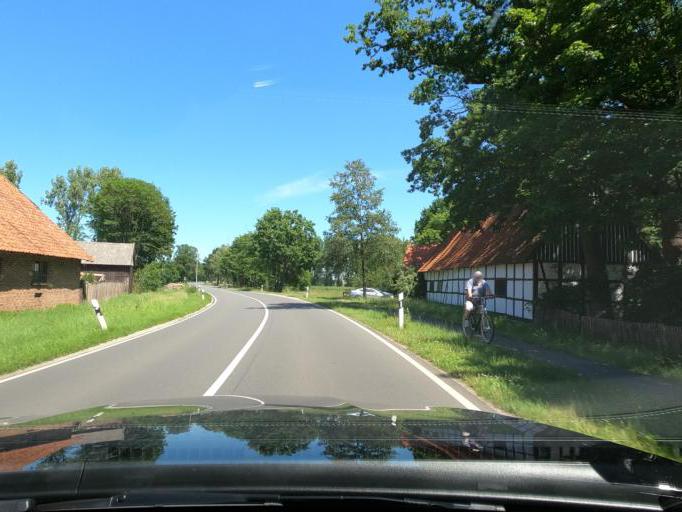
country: DE
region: Lower Saxony
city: Wathlingen
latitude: 52.5419
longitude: 10.1643
